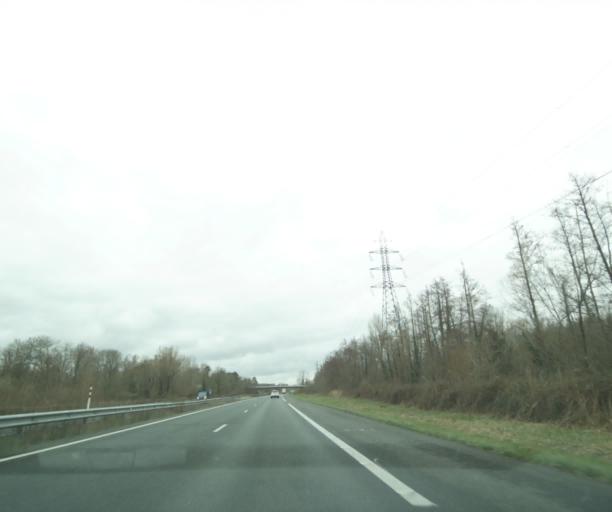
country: FR
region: Aquitaine
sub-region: Departement de la Gironde
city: Saint-Christoly-de-Blaye
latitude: 45.1242
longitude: -0.4857
